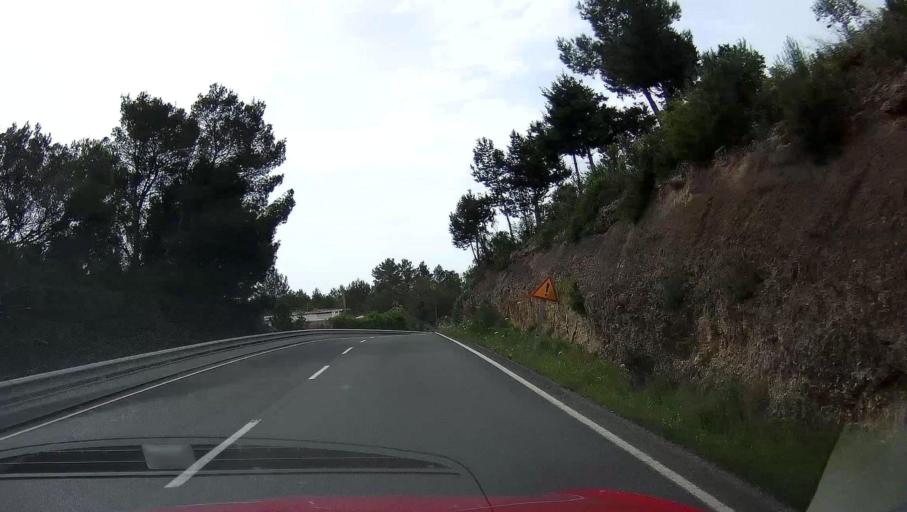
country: ES
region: Balearic Islands
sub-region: Illes Balears
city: Sant Joan de Labritja
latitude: 39.0797
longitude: 1.5025
